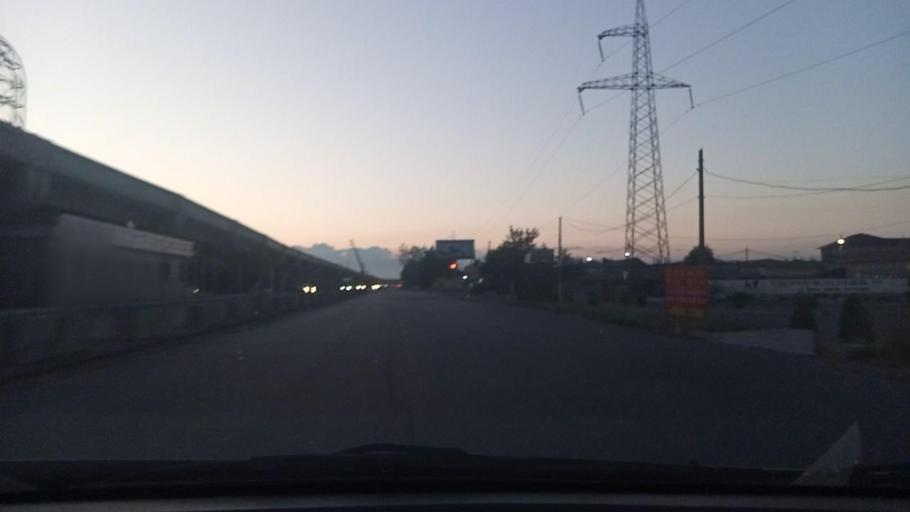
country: UZ
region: Toshkent Shahri
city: Bektemir
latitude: 41.2442
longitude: 69.2998
